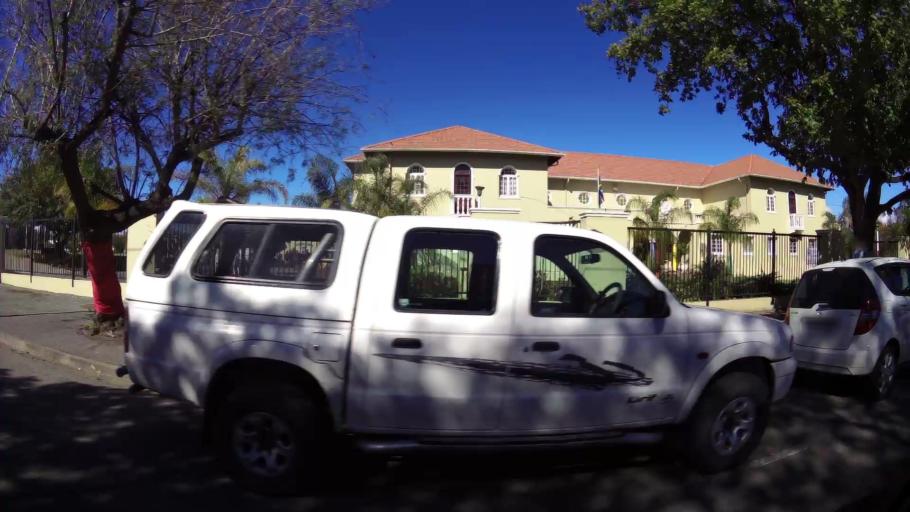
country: ZA
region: Western Cape
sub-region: Cape Winelands District Municipality
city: Ashton
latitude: -33.8054
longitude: 19.8892
